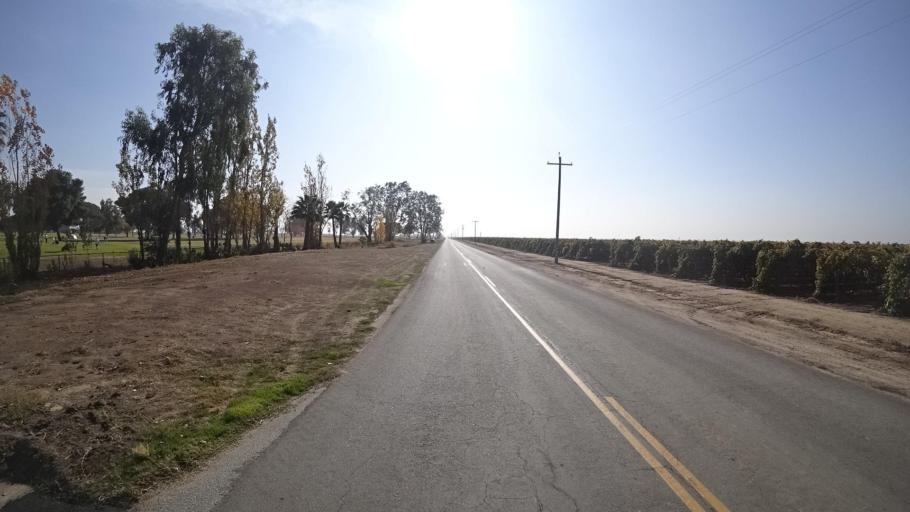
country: US
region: California
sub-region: Kern County
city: Greenacres
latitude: 35.5196
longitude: -119.1162
